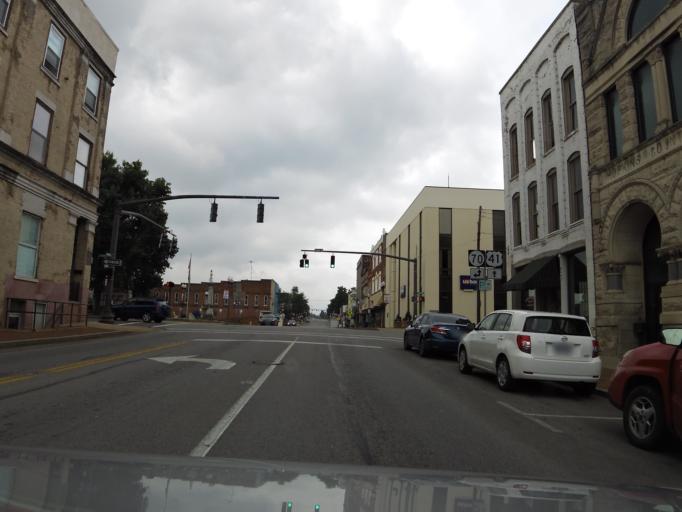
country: US
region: Kentucky
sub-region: Hopkins County
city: Madisonville
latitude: 37.3285
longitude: -87.4989
